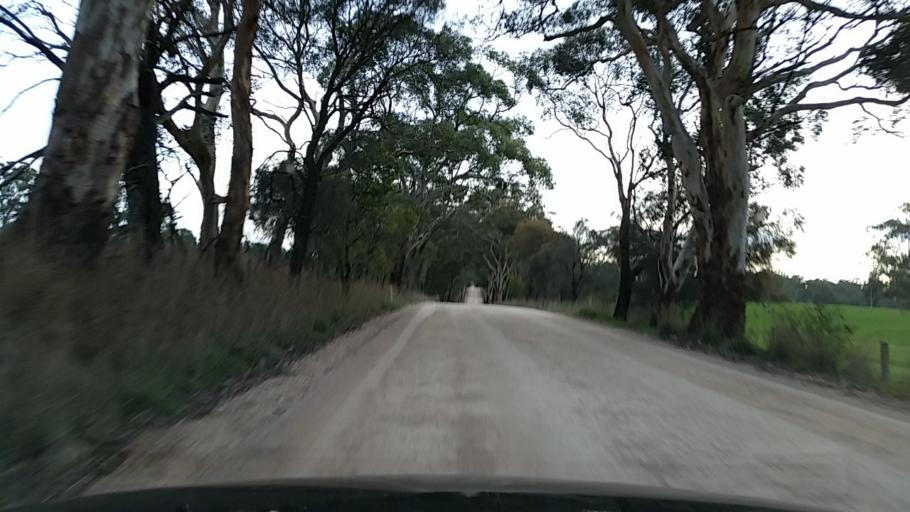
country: AU
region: South Australia
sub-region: Adelaide Hills
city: Birdwood
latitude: -34.8786
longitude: 138.9850
